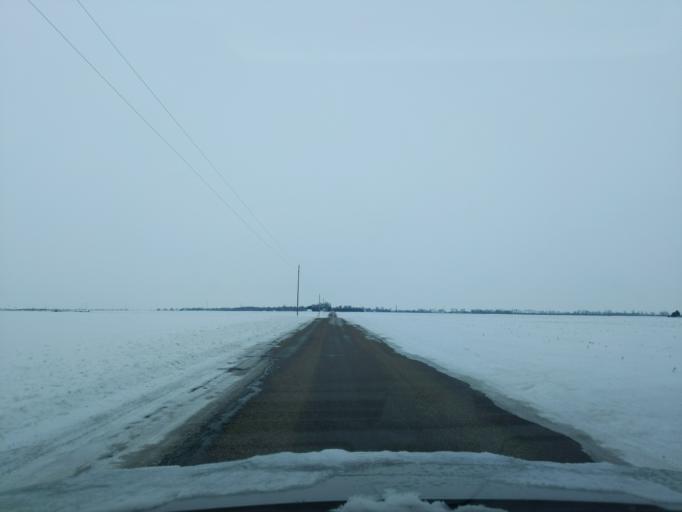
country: US
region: Indiana
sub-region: Benton County
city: Otterbein
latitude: 40.4621
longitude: -87.0928
